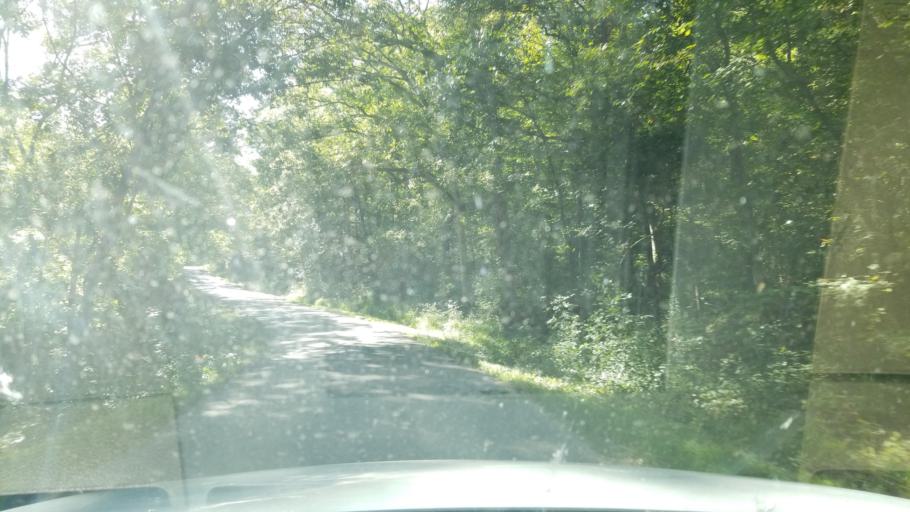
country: US
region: Illinois
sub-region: Hardin County
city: Elizabethtown
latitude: 37.6012
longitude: -88.3781
